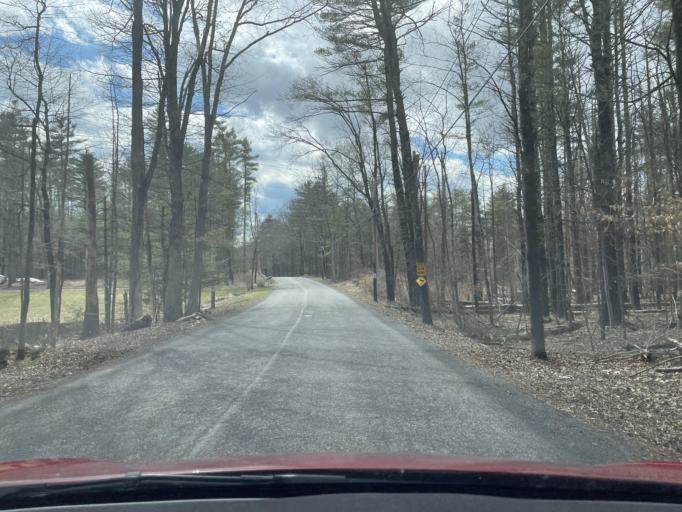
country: US
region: New York
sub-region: Ulster County
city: Zena
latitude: 42.0715
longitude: -74.0326
